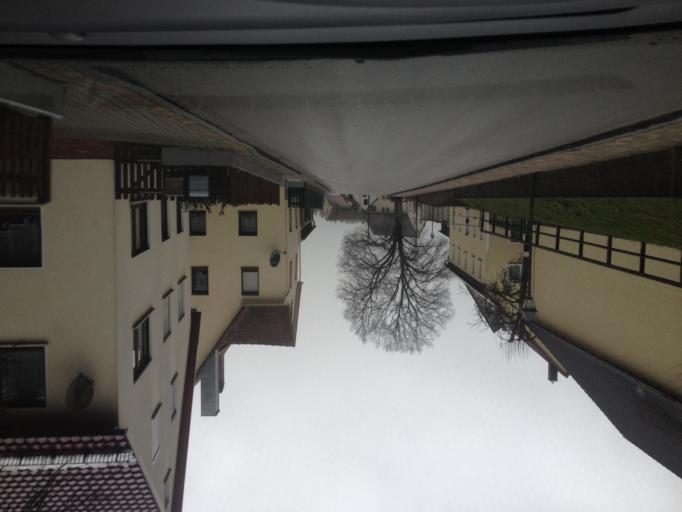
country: DE
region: Bavaria
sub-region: Regierungsbezirk Mittelfranken
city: Lauf an der Pegnitz
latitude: 49.5518
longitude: 11.2687
